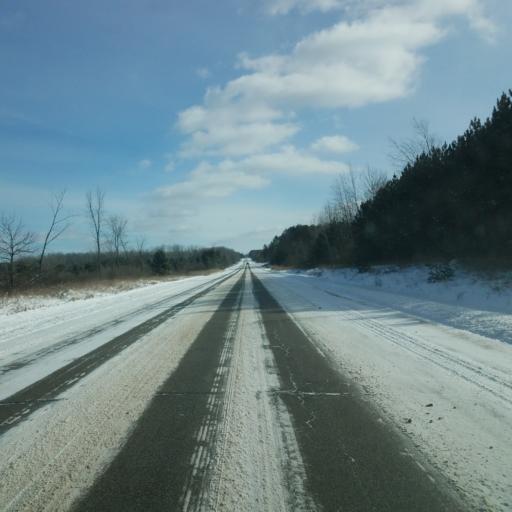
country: US
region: Michigan
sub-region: Osceola County
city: Evart
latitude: 43.9007
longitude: -85.1428
